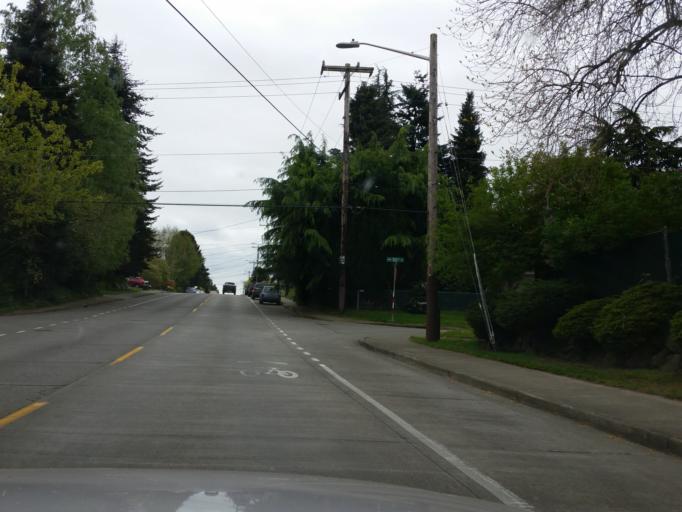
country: US
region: Washington
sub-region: King County
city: Shoreline
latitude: 47.6964
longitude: -122.3661
